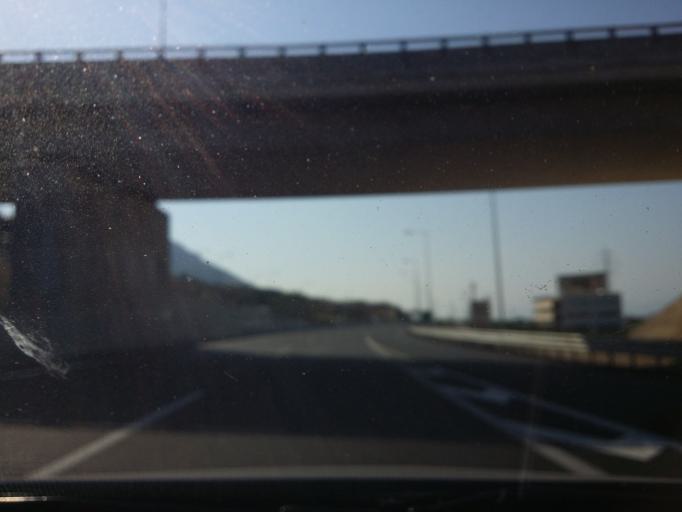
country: GR
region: Peloponnese
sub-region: Nomos Korinthias
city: Xylokastro
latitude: 38.0735
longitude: 22.6138
